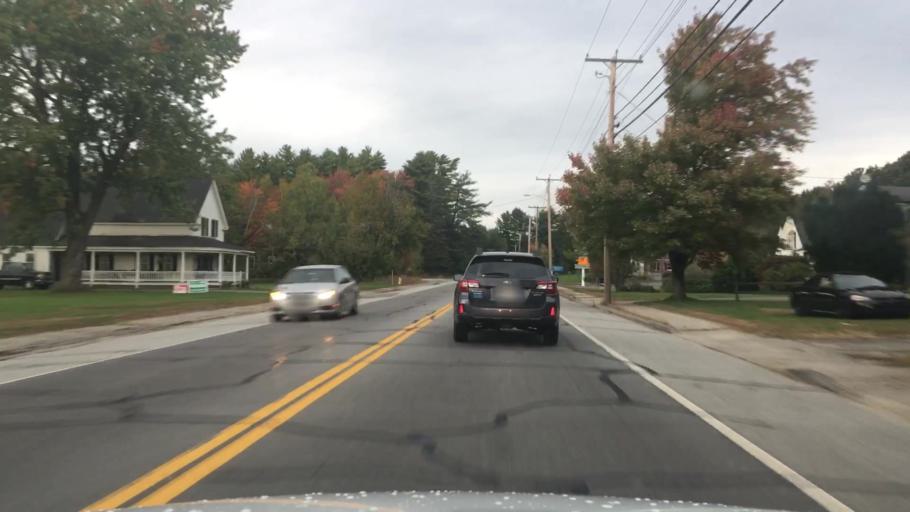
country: US
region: Maine
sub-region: York County
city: Waterboro
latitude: 43.5391
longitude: -70.7118
